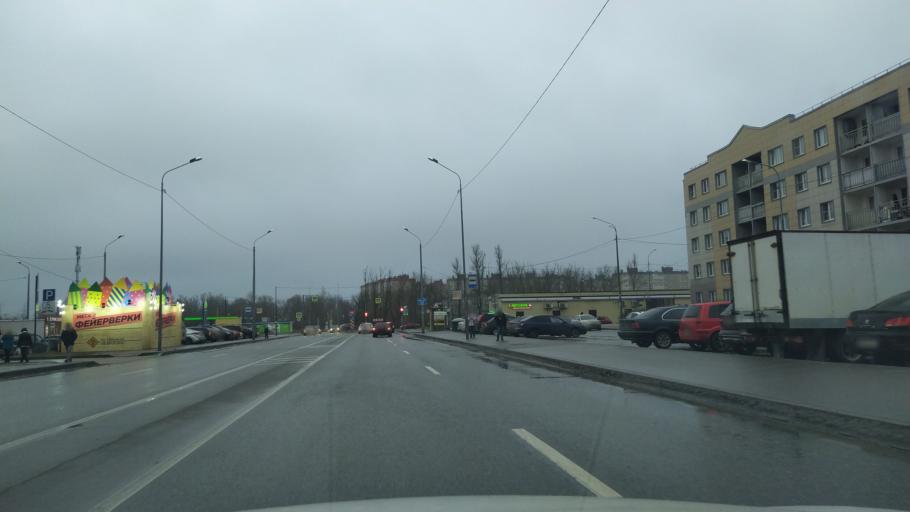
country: RU
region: St.-Petersburg
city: Tyarlevo
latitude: 59.7355
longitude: 30.4701
